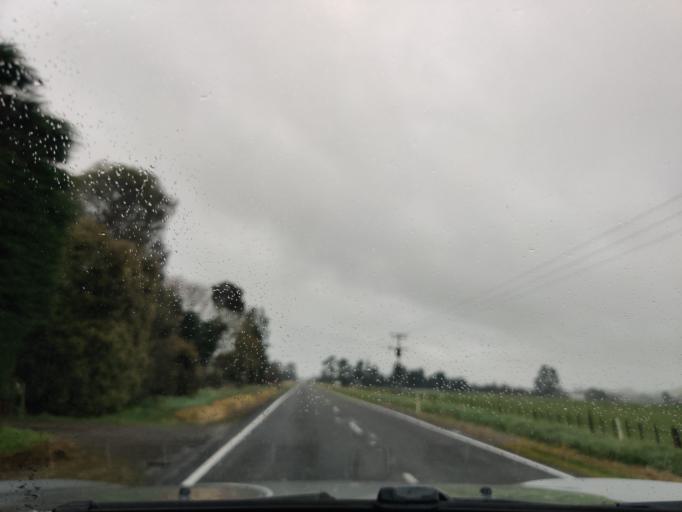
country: NZ
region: Hawke's Bay
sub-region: Hastings District
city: Hastings
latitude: -40.0207
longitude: 176.3374
